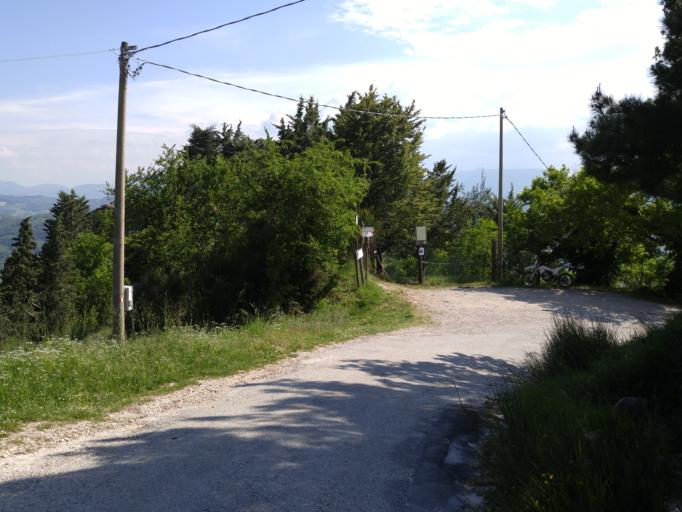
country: IT
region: The Marches
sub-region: Provincia di Pesaro e Urbino
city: Acqualagna
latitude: 43.6517
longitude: 12.6946
